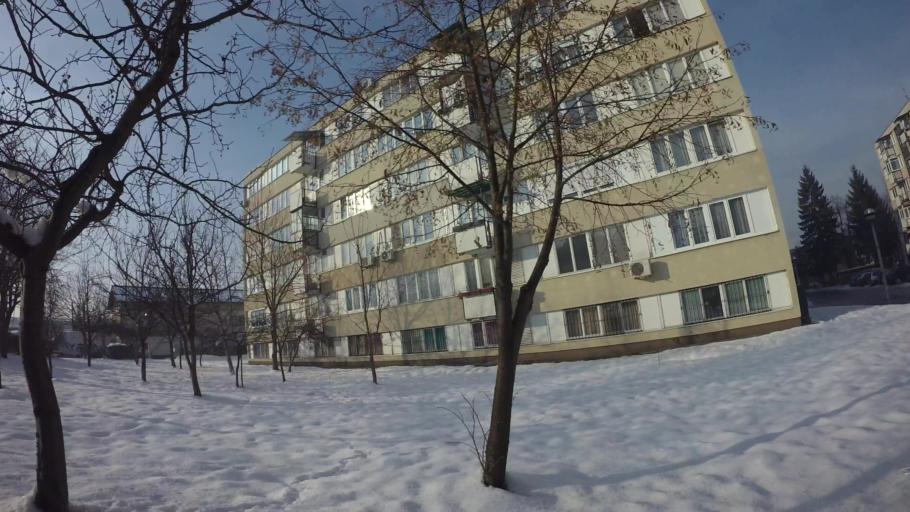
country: BA
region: Federation of Bosnia and Herzegovina
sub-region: Kanton Sarajevo
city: Sarajevo
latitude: 43.8452
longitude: 18.3695
